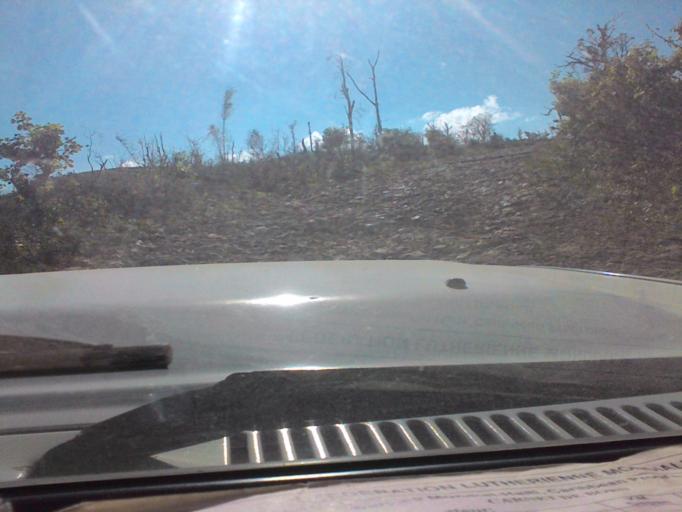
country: HT
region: Grandans
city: Jeremie
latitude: 18.4929
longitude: -74.1076
